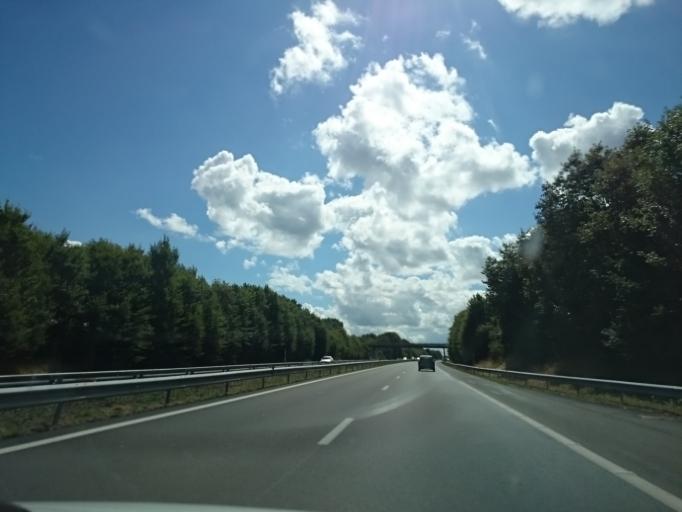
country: FR
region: Pays de la Loire
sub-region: Departement de Maine-et-Loire
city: Durtal
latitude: 47.6826
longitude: -0.2527
